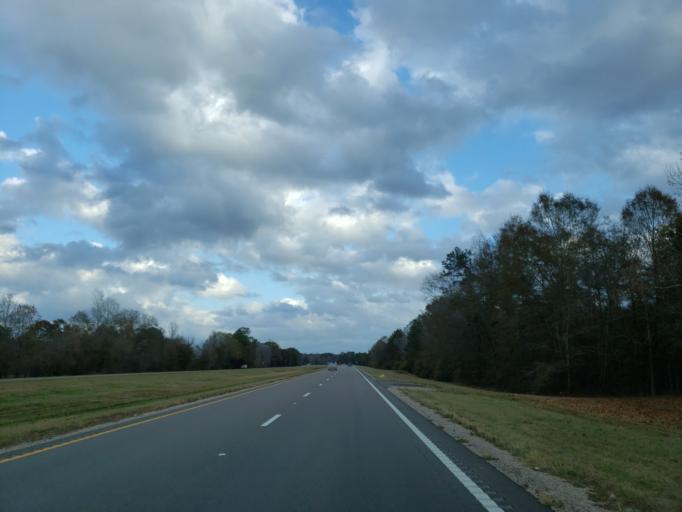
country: US
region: Mississippi
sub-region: Perry County
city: New Augusta
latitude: 31.2031
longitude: -89.0536
